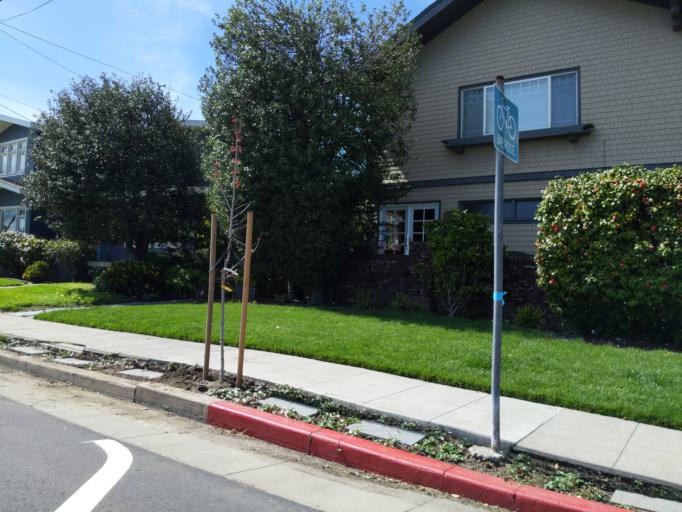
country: US
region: California
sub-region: Alameda County
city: Alameda
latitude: 37.7578
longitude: -122.2268
